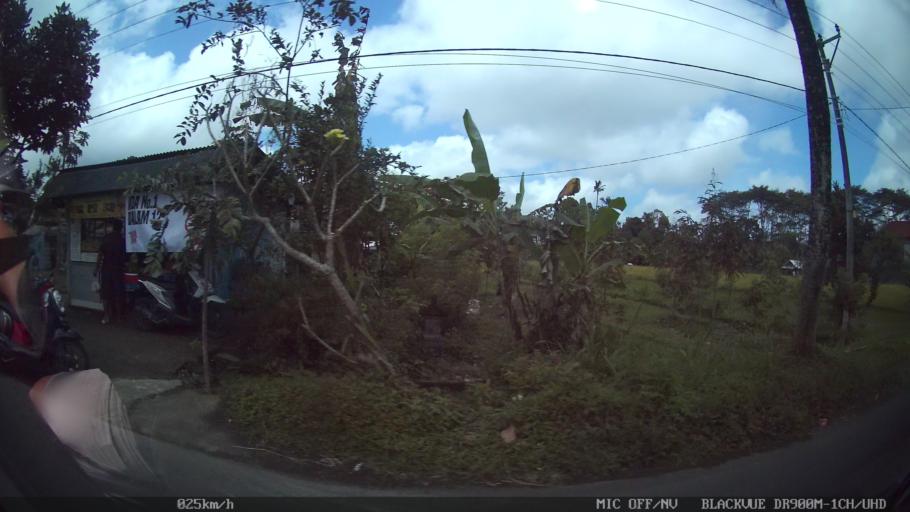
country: ID
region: Bali
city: Banjar Abuan
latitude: -8.4578
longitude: 115.3404
